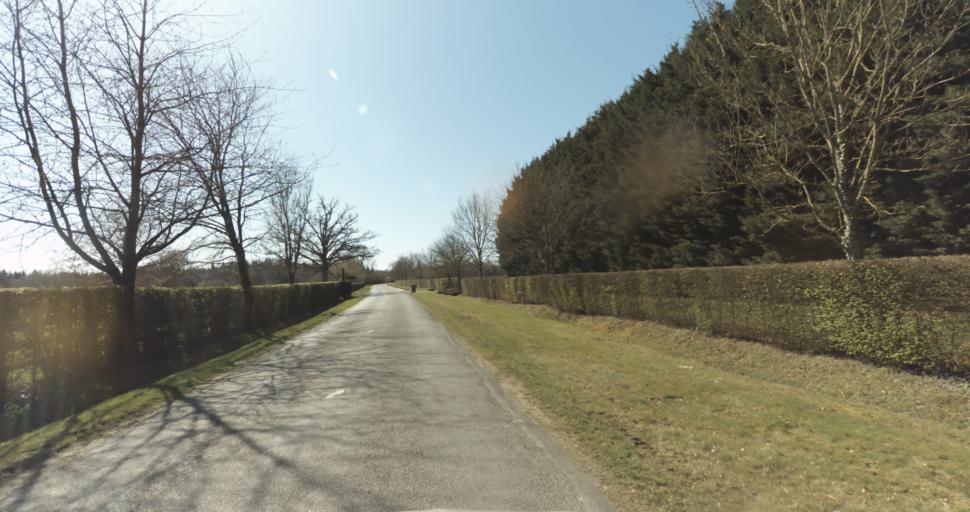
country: FR
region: Lower Normandy
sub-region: Departement du Calvados
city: Livarot
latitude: 48.9561
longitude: 0.0917
